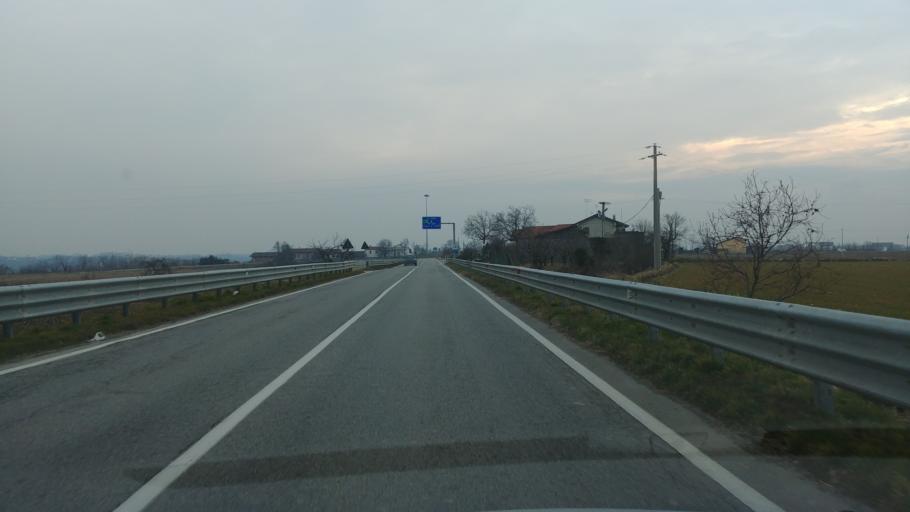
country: IT
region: Piedmont
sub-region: Provincia di Cuneo
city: Castelletto Stura
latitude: 44.4612
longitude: 7.6300
